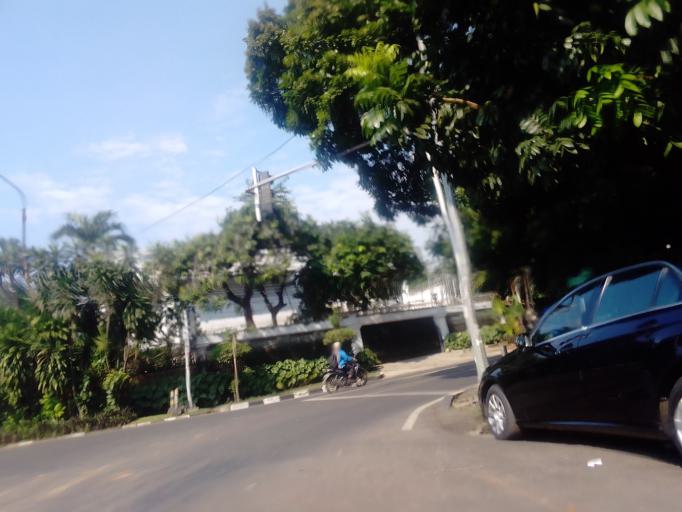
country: ID
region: Jakarta Raya
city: Jakarta
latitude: -6.2544
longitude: 106.8050
